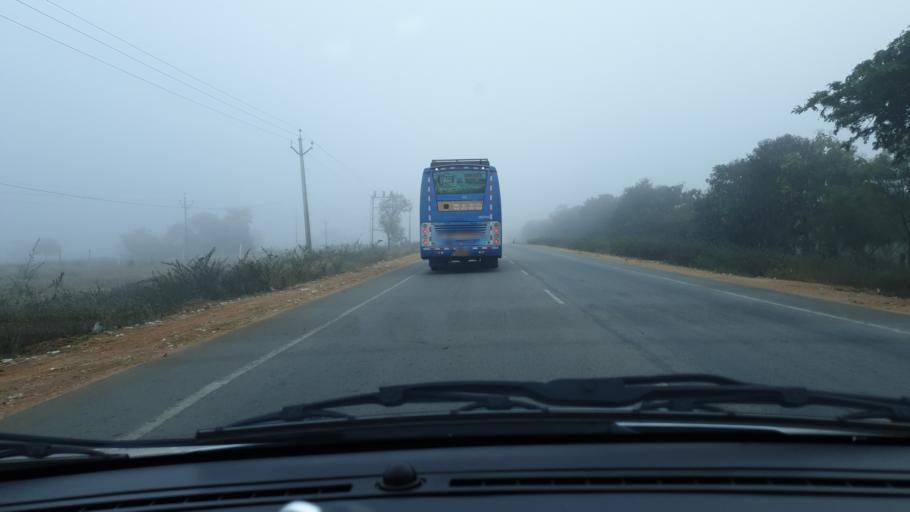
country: IN
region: Telangana
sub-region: Mahbubnagar
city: Nagar Karnul
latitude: 16.6643
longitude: 78.5469
